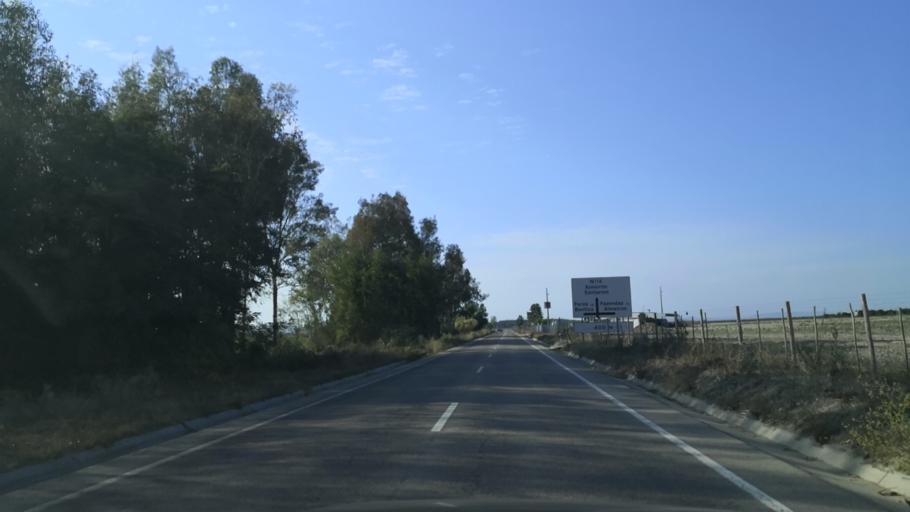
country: PT
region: Santarem
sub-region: Almeirim
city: Fazendas de Almeirim
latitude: 39.1487
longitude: -8.6168
